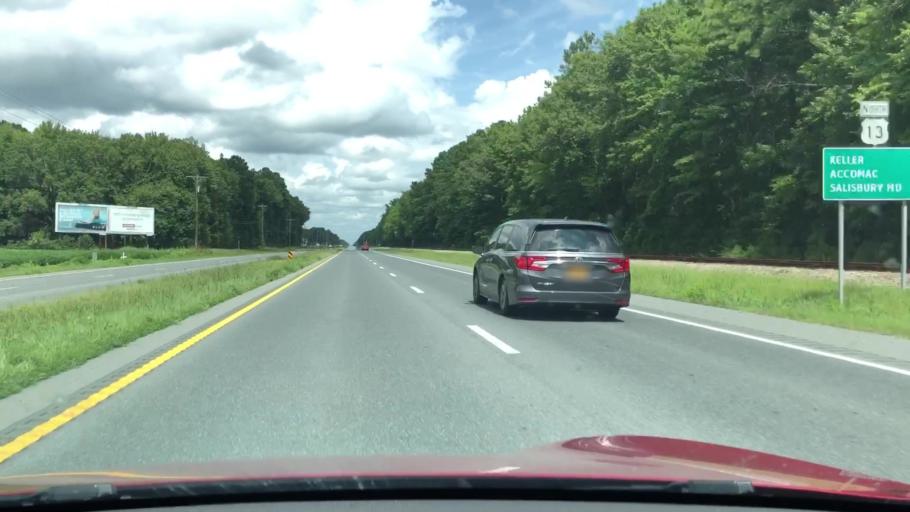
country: US
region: Virginia
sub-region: Northampton County
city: Exmore
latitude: 37.5922
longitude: -75.7807
